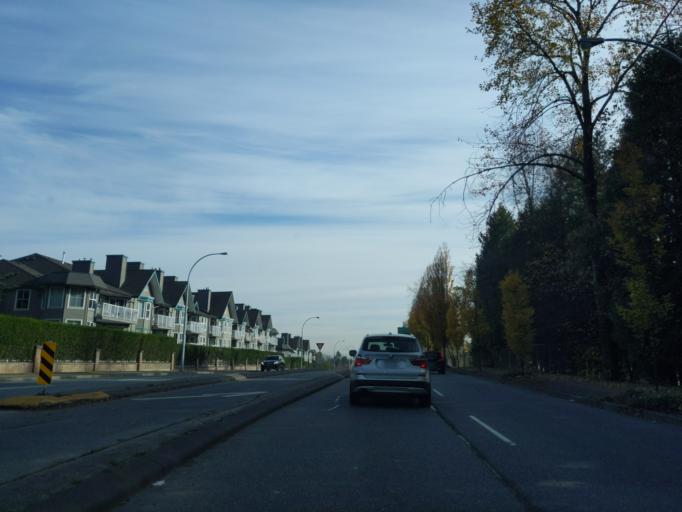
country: CA
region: British Columbia
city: Surrey
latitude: 49.1985
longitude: -122.8039
